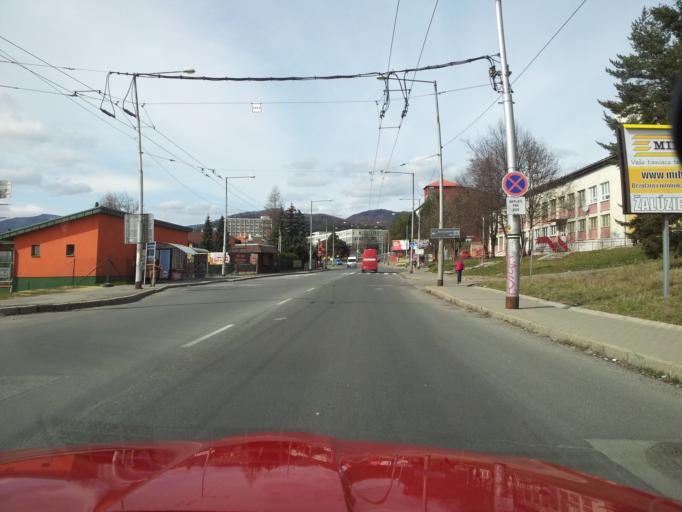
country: SK
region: Banskobystricky
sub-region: Okres Banska Bystrica
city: Banska Bystrica
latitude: 48.7397
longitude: 19.1273
